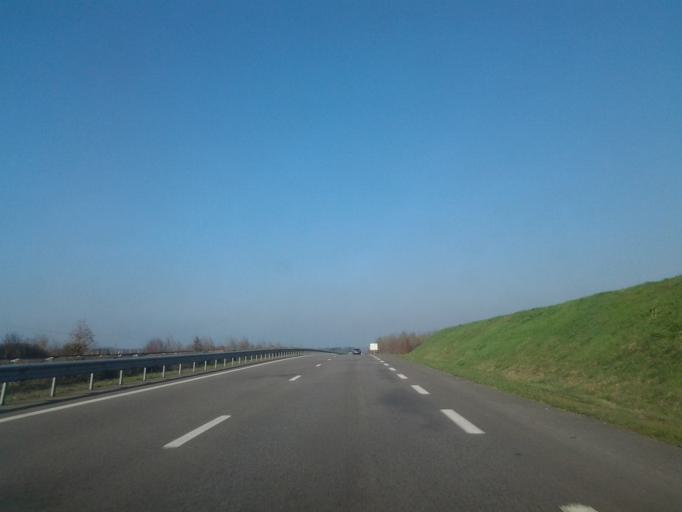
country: FR
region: Pays de la Loire
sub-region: Departement de la Vendee
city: Mache
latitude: 46.7943
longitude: -1.7139
